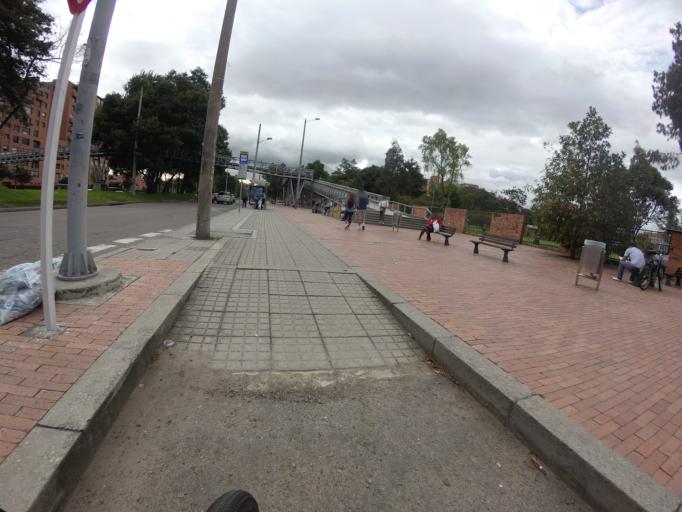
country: CO
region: Bogota D.C.
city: Barrio San Luis
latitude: 4.7042
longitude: -74.0350
